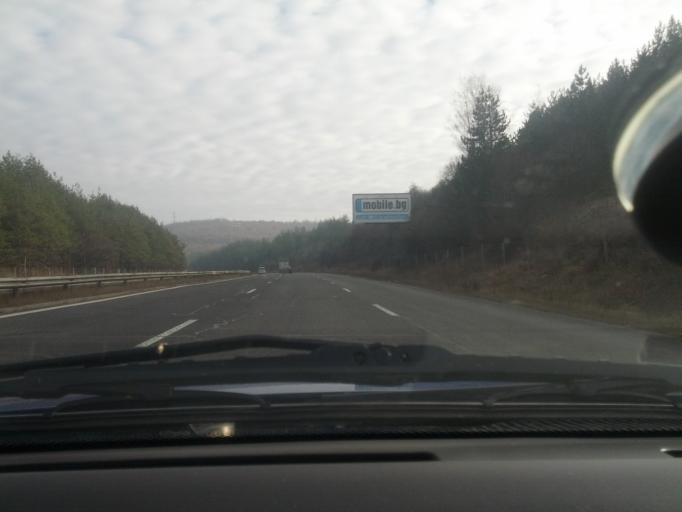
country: BG
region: Sofiya
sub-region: Obshtina Gorna Malina
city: Gorna Malina
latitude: 42.7376
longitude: 23.6480
